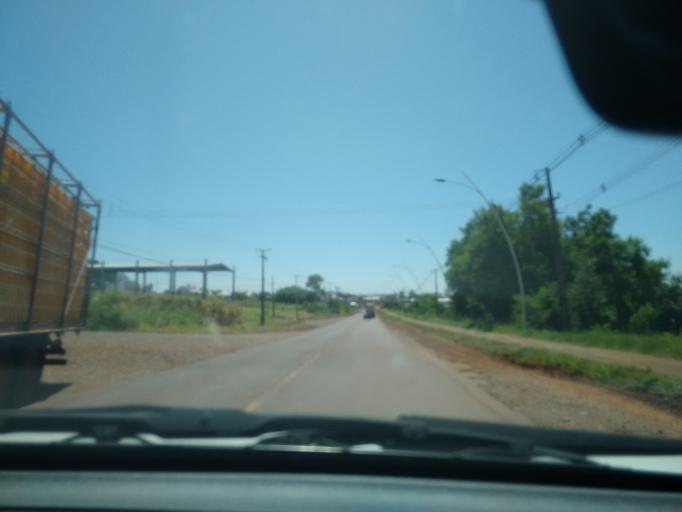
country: BR
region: Parana
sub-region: Marechal Candido Rondon
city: Marechal Candido Rondon
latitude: -24.5570
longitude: -54.0951
